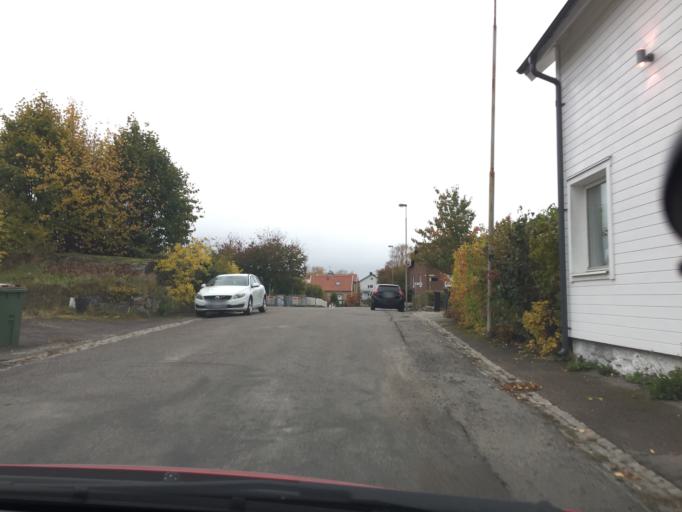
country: SE
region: Vaestra Goetaland
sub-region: Trollhattan
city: Trollhattan
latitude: 58.2862
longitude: 12.3157
